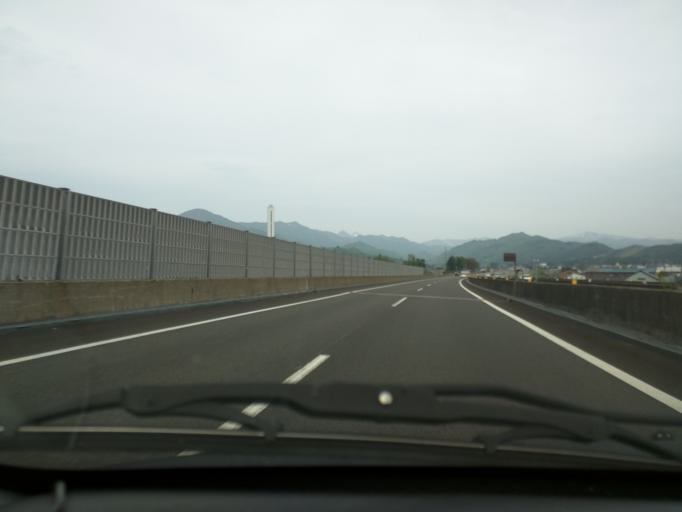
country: JP
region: Niigata
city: Ojiya
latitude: 37.2438
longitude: 138.9561
